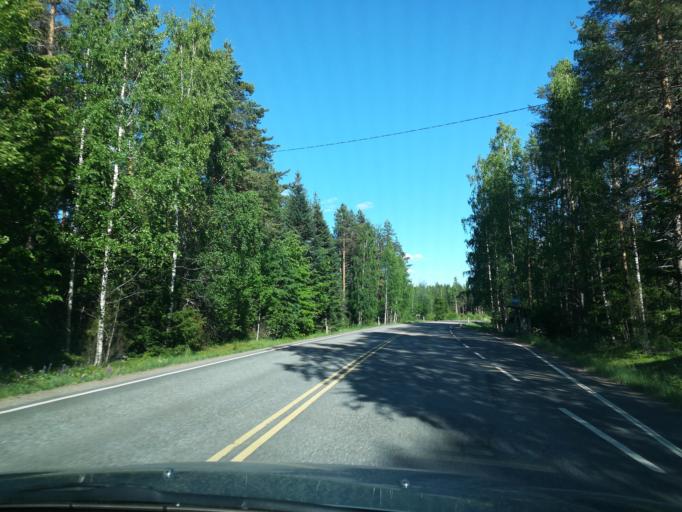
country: FI
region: South Karelia
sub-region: Imatra
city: Ruokolahti
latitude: 61.3993
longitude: 28.6261
